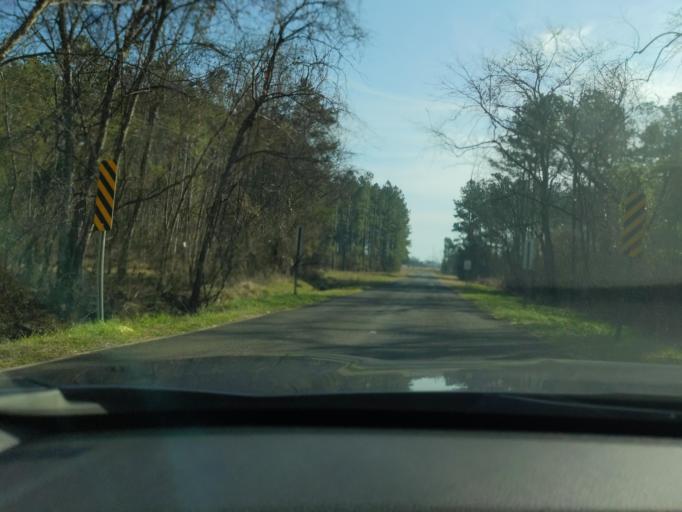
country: US
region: South Carolina
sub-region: Abbeville County
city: Calhoun Falls
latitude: 34.0813
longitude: -82.5729
